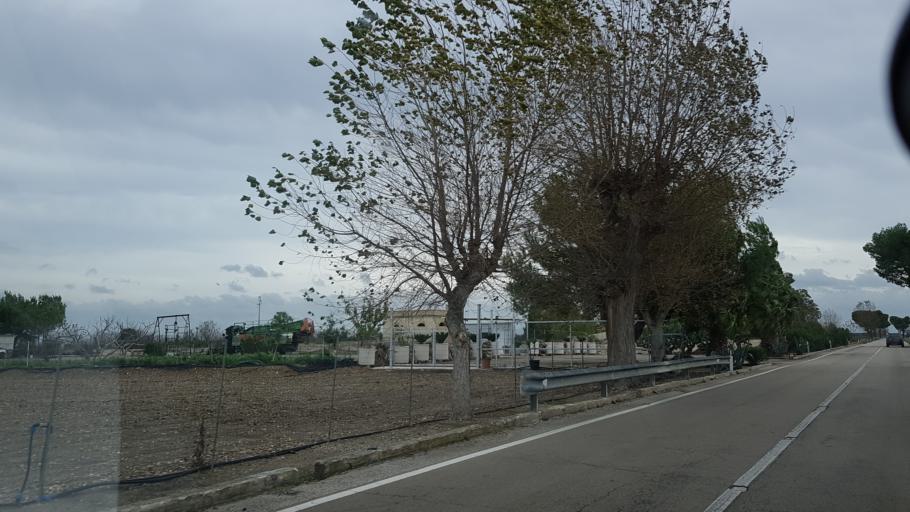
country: IT
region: Apulia
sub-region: Provincia di Brindisi
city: San Pancrazio Salentino
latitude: 40.4126
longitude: 17.8623
